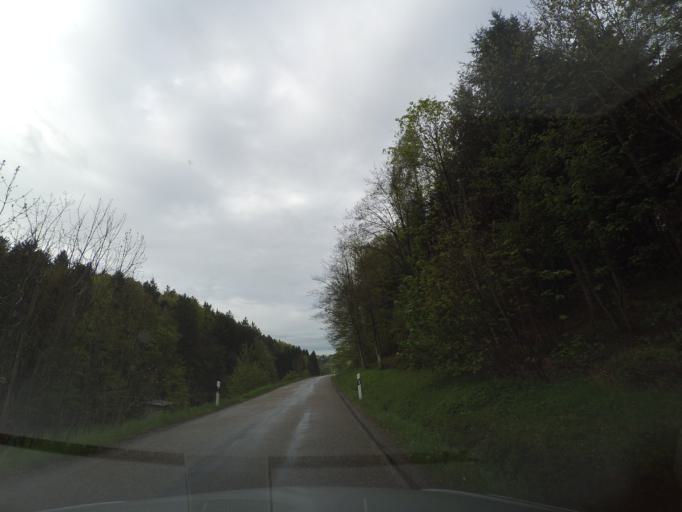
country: DE
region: Baden-Wuerttemberg
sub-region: Regierungsbezirk Stuttgart
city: Mainhardt
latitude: 49.0318
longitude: 9.5733
